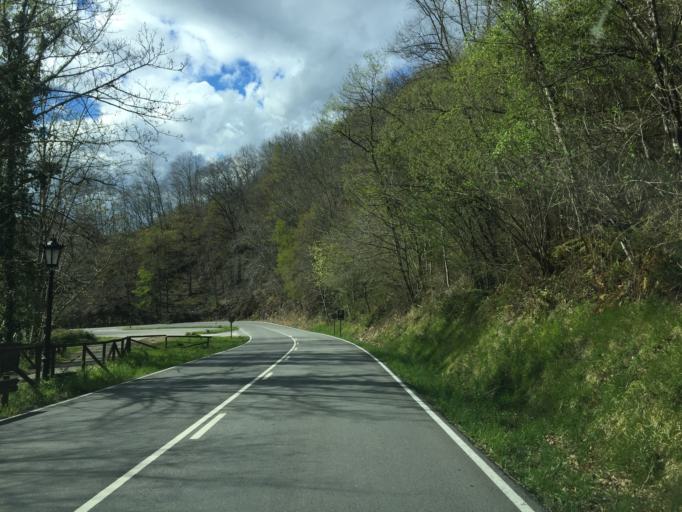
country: ES
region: Asturias
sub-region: Province of Asturias
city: Amieva
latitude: 43.3108
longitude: -5.0534
